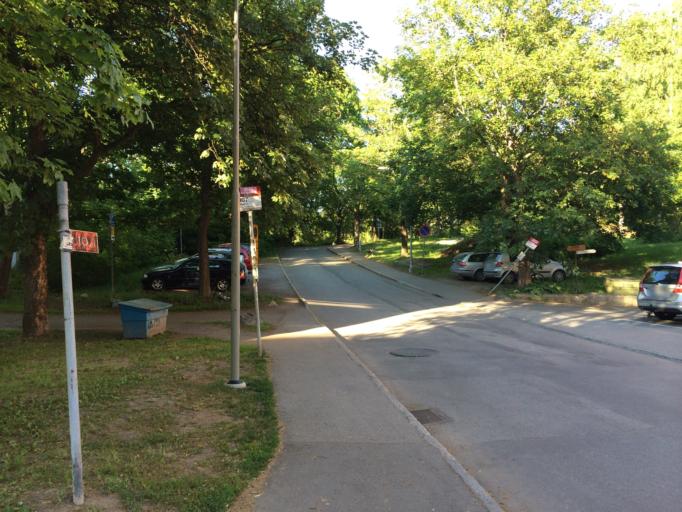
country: SE
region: Stockholm
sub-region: Huddinge Kommun
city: Segeltorp
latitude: 59.2935
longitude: 17.9672
